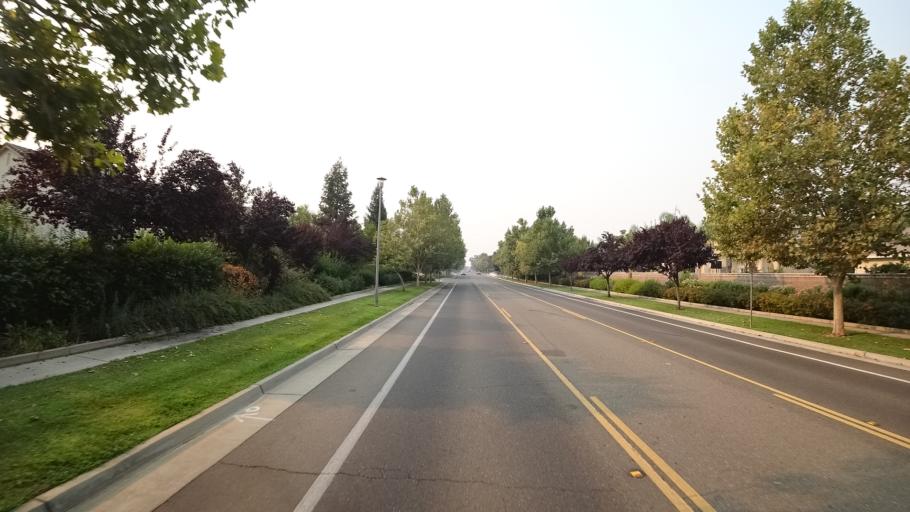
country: US
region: California
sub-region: Sacramento County
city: Laguna
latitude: 38.4066
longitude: -121.4408
